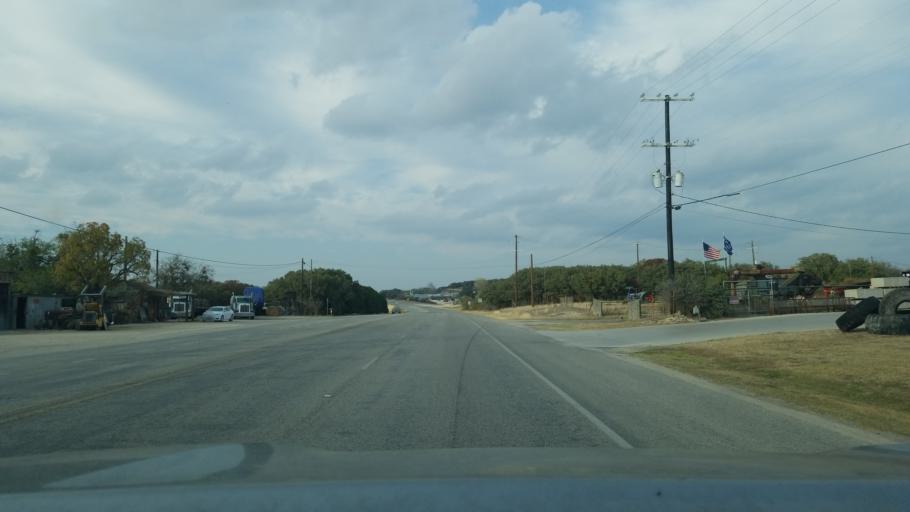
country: US
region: Texas
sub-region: Mills County
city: Goldthwaite
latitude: 31.4740
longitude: -98.5687
